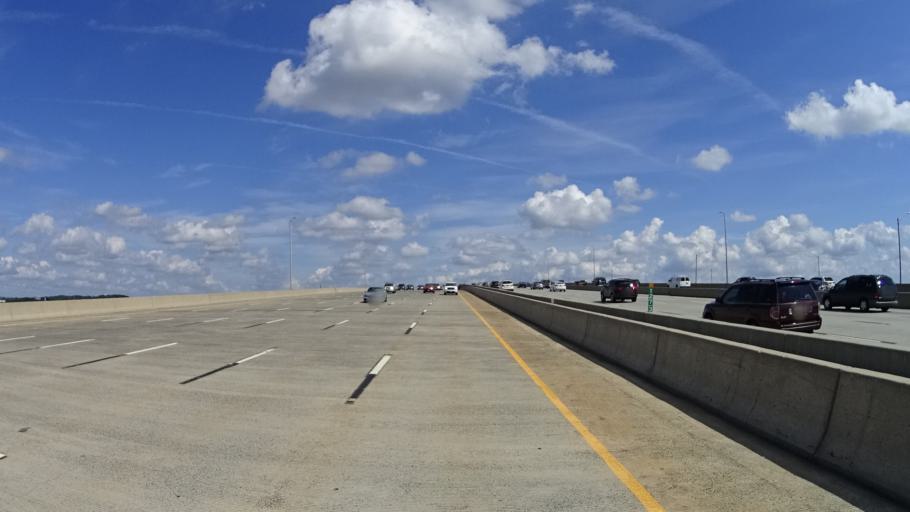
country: US
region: New Jersey
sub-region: Middlesex County
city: Fords
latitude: 40.5085
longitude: -74.3013
